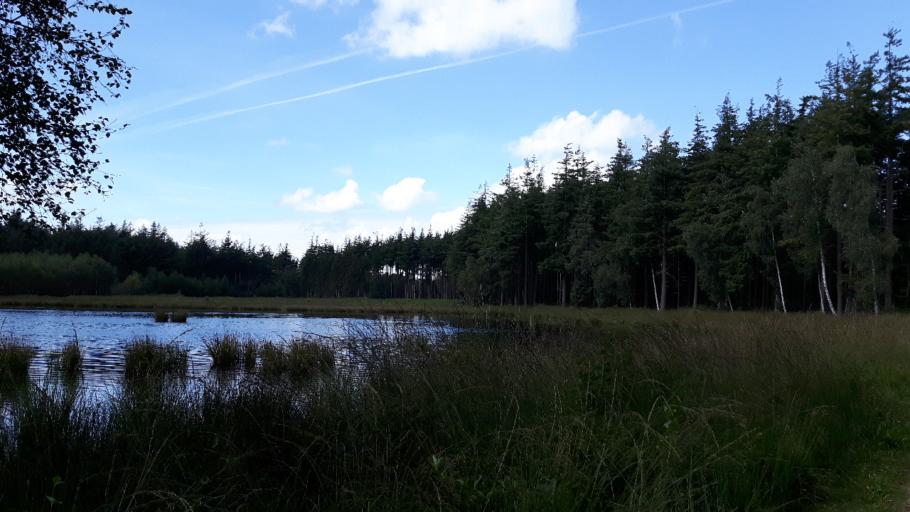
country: NL
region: Friesland
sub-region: Gemeente Smallingerland
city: Drachtstercompagnie
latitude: 53.0766
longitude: 6.2466
